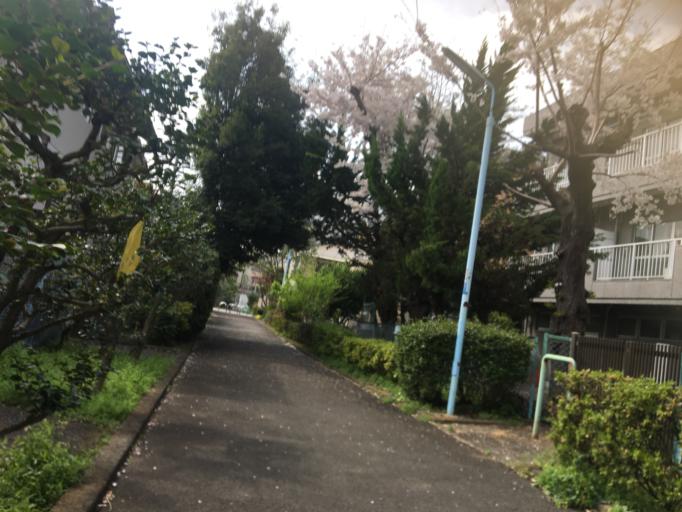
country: JP
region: Tokyo
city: Musashino
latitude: 35.7242
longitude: 139.6131
